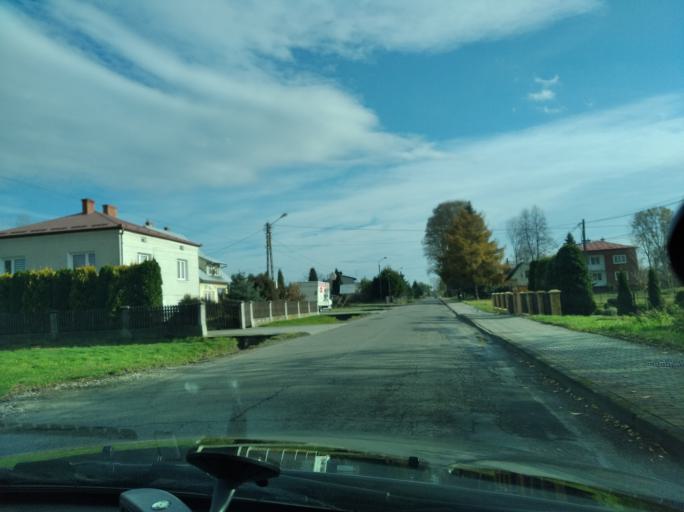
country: PL
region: Subcarpathian Voivodeship
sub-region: Powiat ropczycko-sedziszowski
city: Ostrow
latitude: 50.0995
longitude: 21.6152
